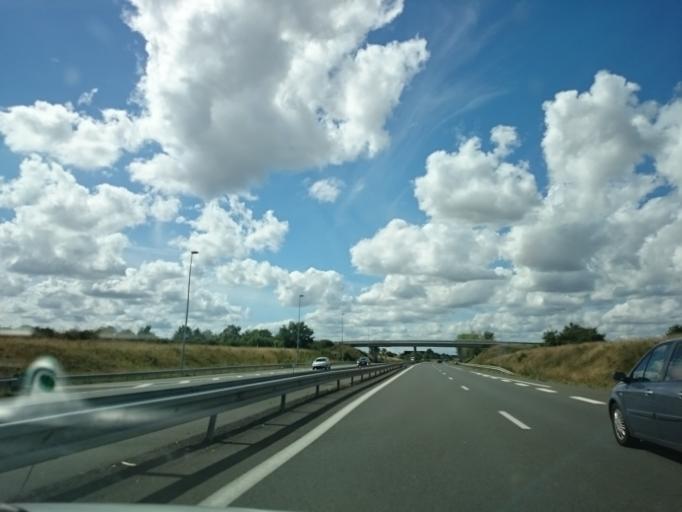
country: FR
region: Pays de la Loire
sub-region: Departement de Maine-et-Loire
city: Saint-Germain-des-Pres
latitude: 47.4344
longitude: -0.8151
